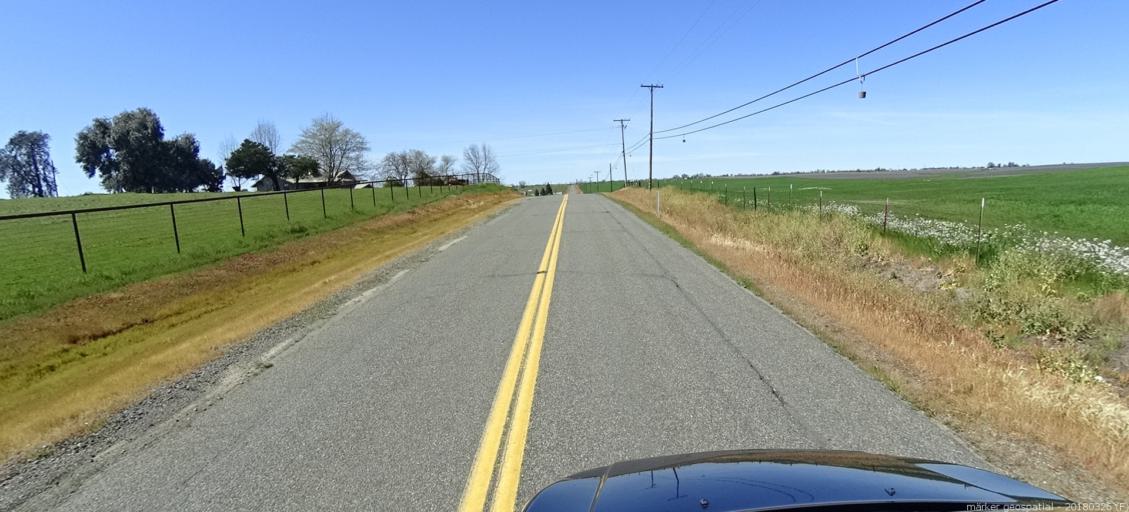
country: US
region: California
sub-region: Sacramento County
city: Wilton
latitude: 38.4656
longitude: -121.2442
